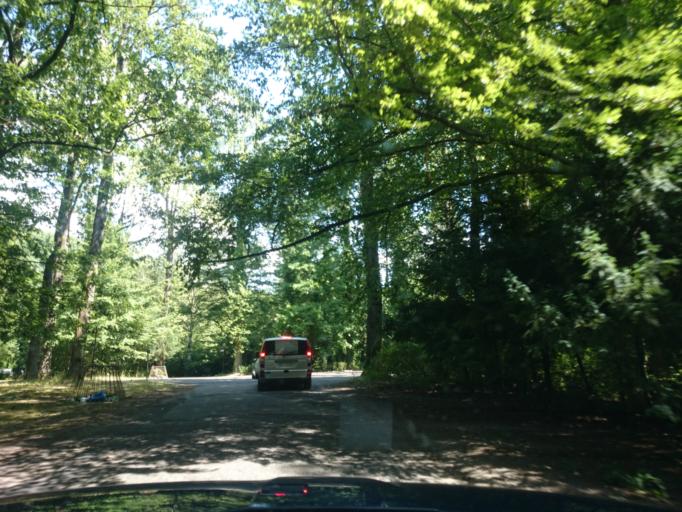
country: PL
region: West Pomeranian Voivodeship
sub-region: Szczecin
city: Szczecin
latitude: 53.4149
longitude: 14.5177
